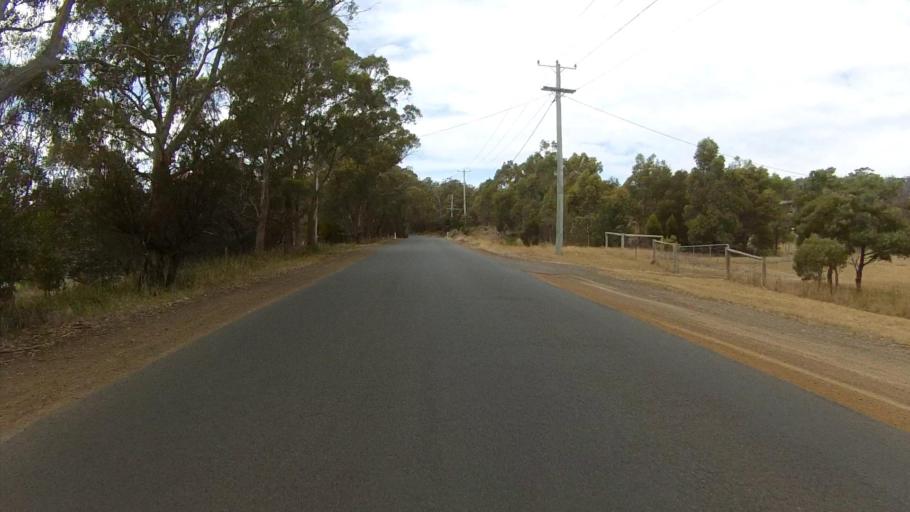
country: AU
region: Tasmania
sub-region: Kingborough
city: Blackmans Bay
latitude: -43.0234
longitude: 147.3059
